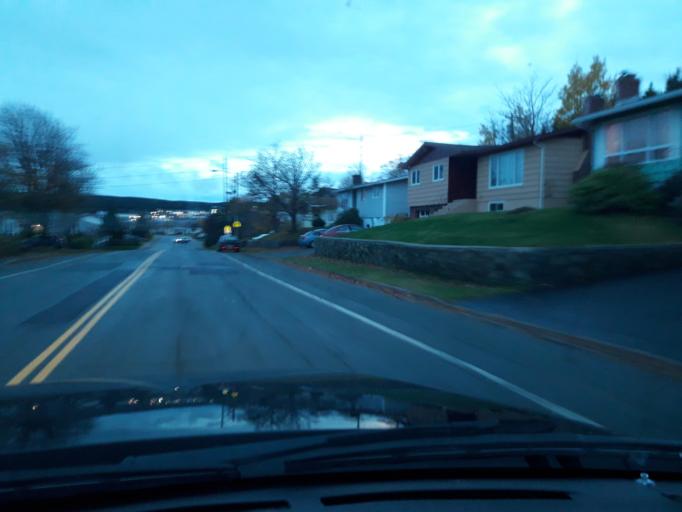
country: CA
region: Newfoundland and Labrador
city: St. John's
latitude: 47.5665
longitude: -52.7522
